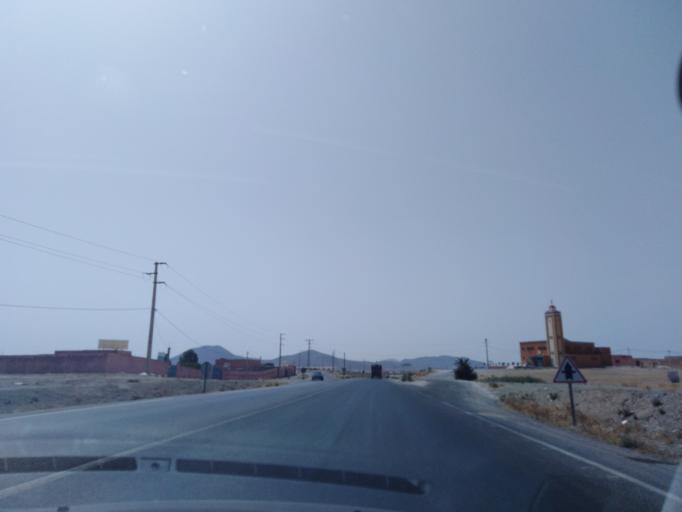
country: MA
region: Marrakech-Tensift-Al Haouz
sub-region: Marrakech
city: Marrakesh
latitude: 31.7738
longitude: -8.1313
